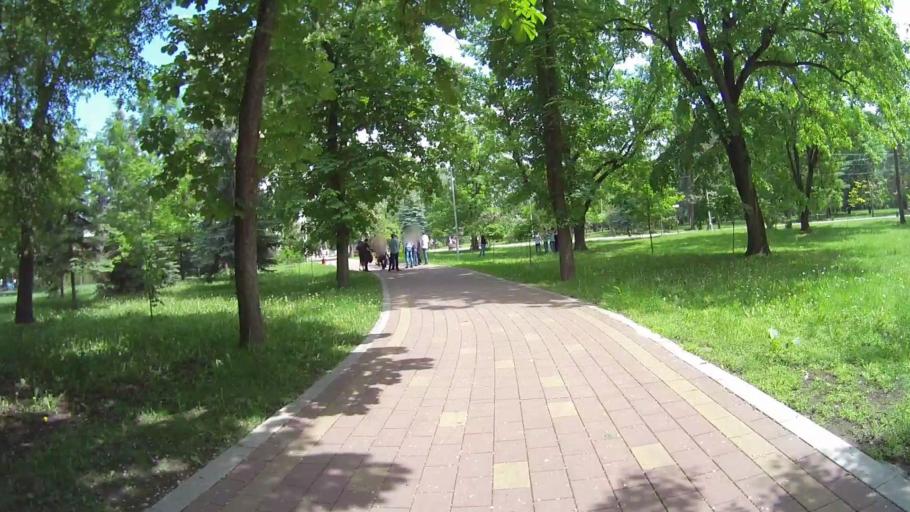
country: RU
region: Kabardino-Balkariya
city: Vol'nyy Aul
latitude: 43.4759
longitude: 43.6020
